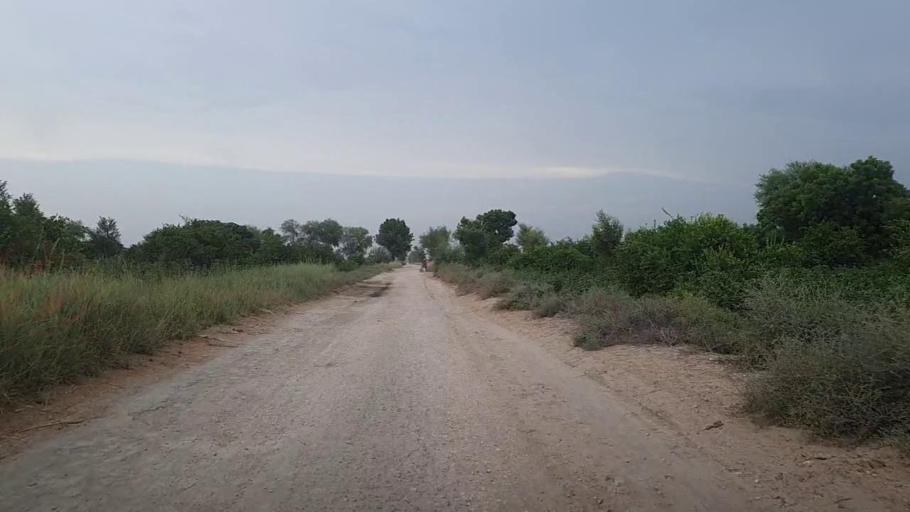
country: PK
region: Sindh
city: Karaundi
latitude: 26.9613
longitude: 68.3438
